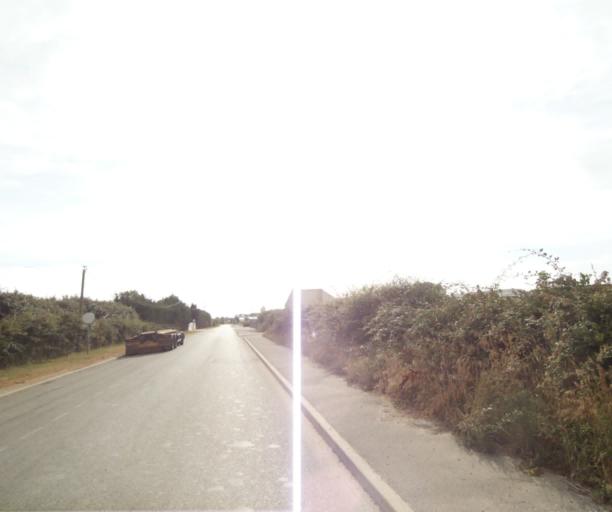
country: FR
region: Pays de la Loire
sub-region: Departement de la Vendee
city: Chateau-d'Olonne
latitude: 46.4930
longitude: -1.7254
